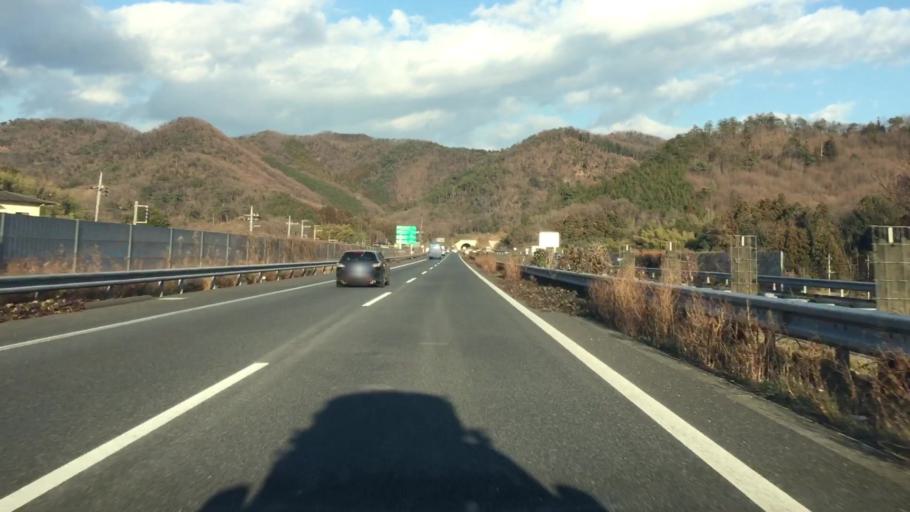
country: JP
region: Tochigi
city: Ashikaga
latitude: 36.3653
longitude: 139.4945
